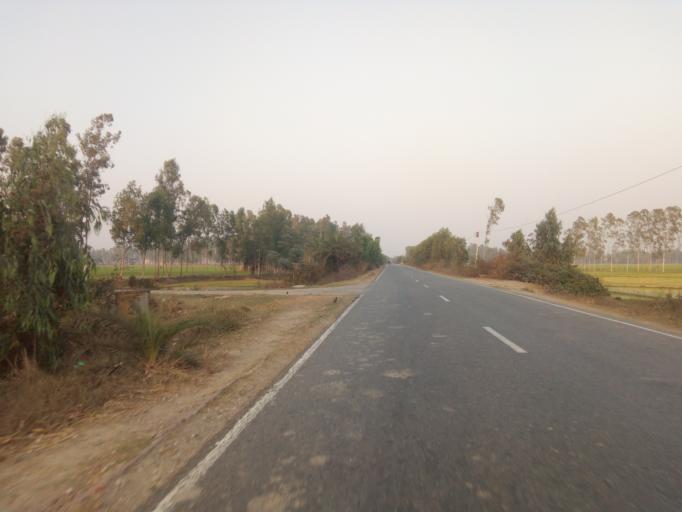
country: BD
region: Rajshahi
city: Bogra
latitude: 24.5824
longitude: 89.2265
